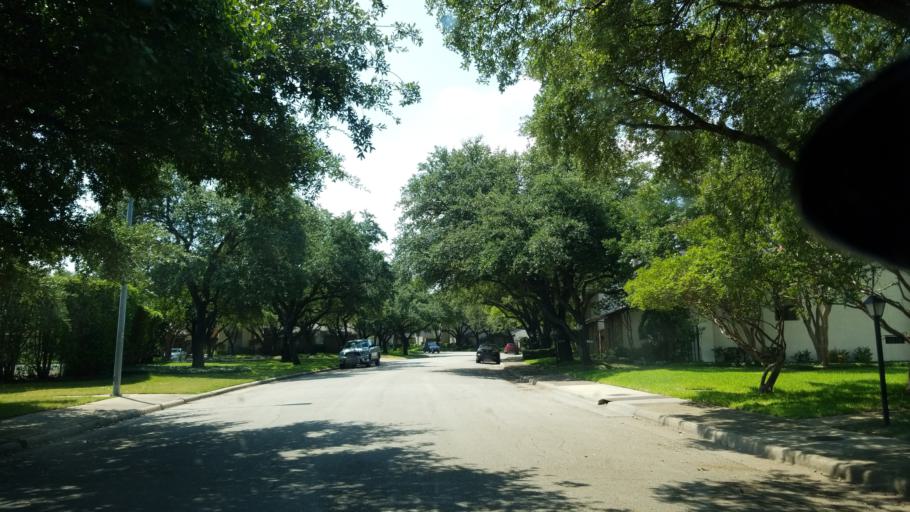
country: US
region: Texas
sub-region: Dallas County
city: Richardson
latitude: 32.9218
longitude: -96.7378
